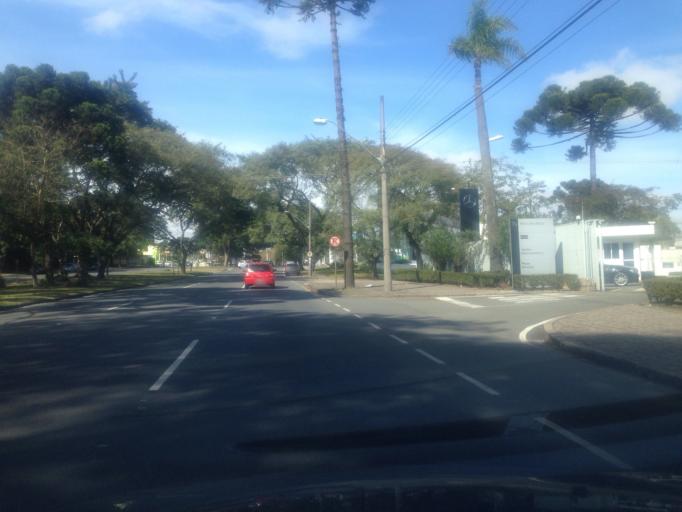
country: BR
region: Parana
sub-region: Curitiba
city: Curitiba
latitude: -25.4187
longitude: -49.2406
